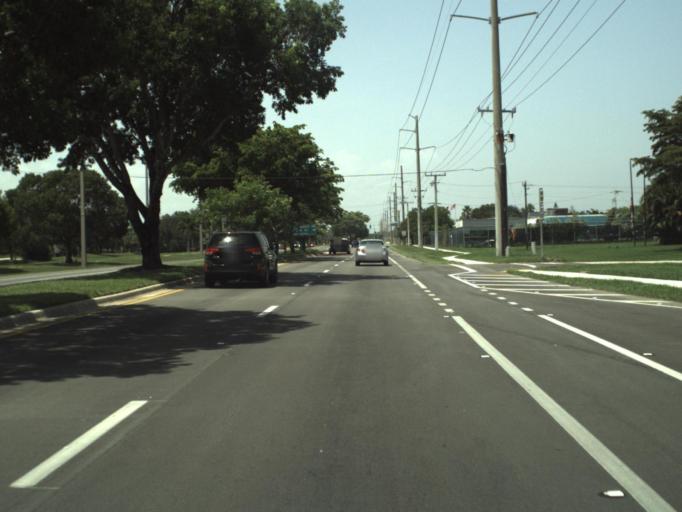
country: US
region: Florida
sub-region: Palm Beach County
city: Boca Pointe
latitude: 26.3089
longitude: -80.1525
